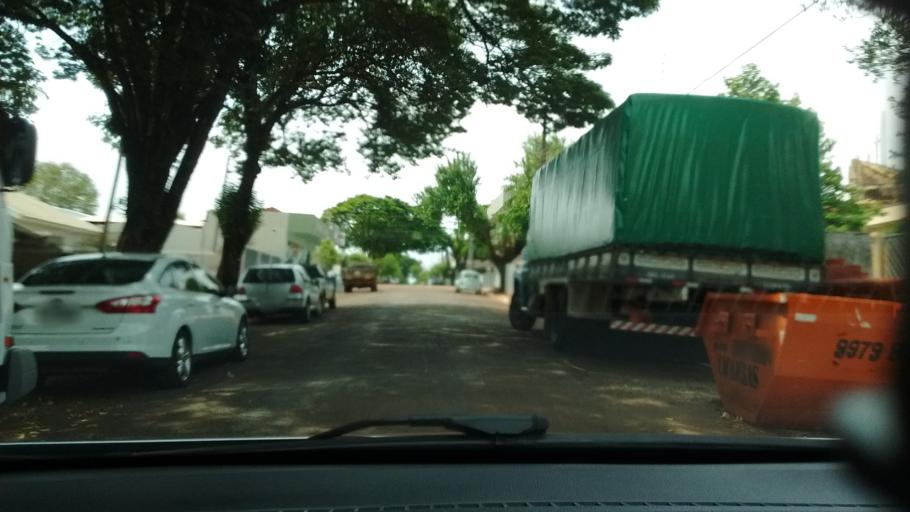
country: BR
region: Parana
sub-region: Corbelia
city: Corbelia
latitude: -24.5451
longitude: -52.9908
